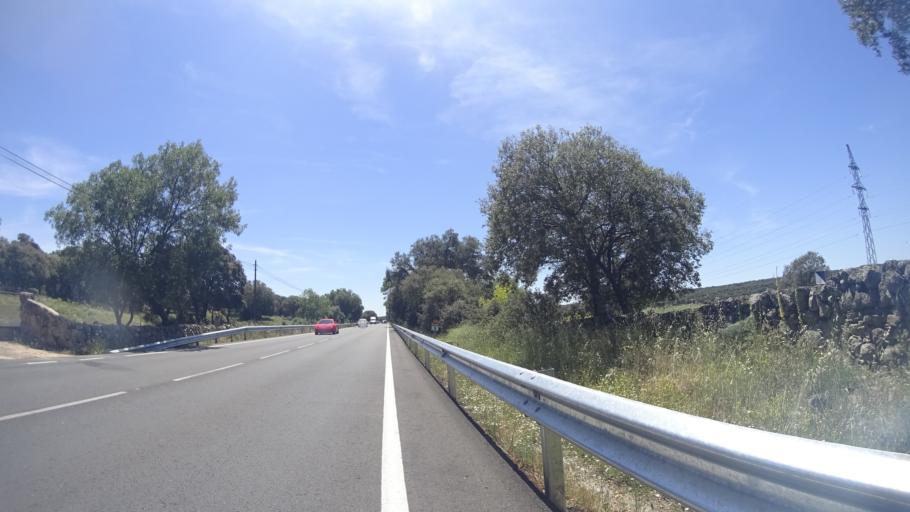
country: ES
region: Madrid
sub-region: Provincia de Madrid
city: Galapagar
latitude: 40.5989
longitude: -4.0183
